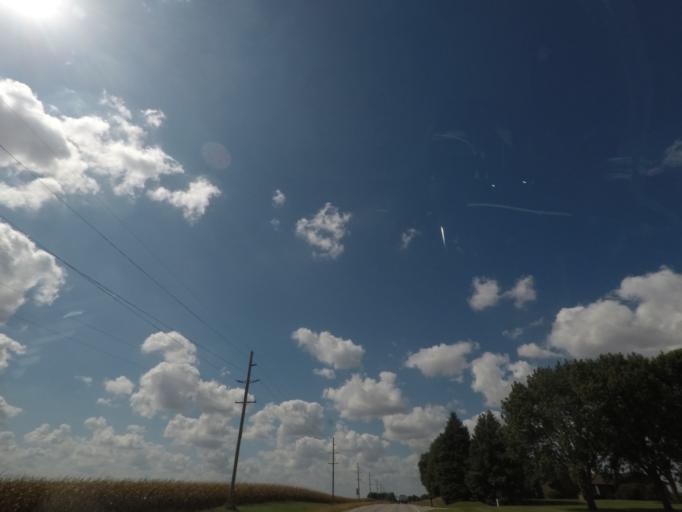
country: US
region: Iowa
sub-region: Story County
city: Nevada
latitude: 42.0226
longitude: -93.4061
